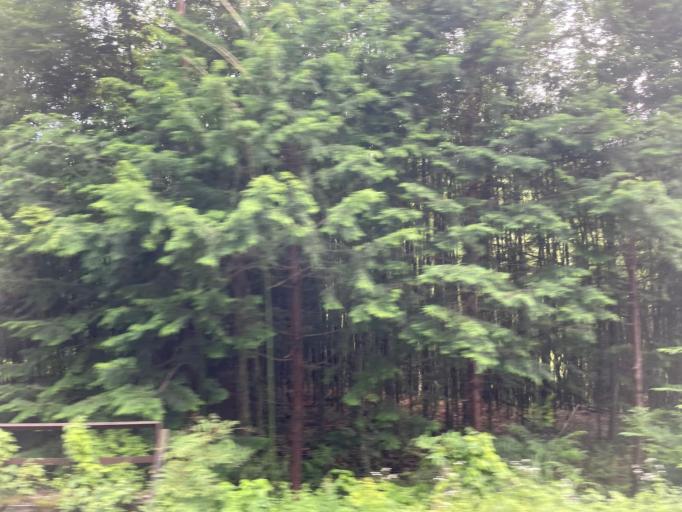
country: JP
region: Gunma
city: Numata
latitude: 36.7461
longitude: 138.9843
